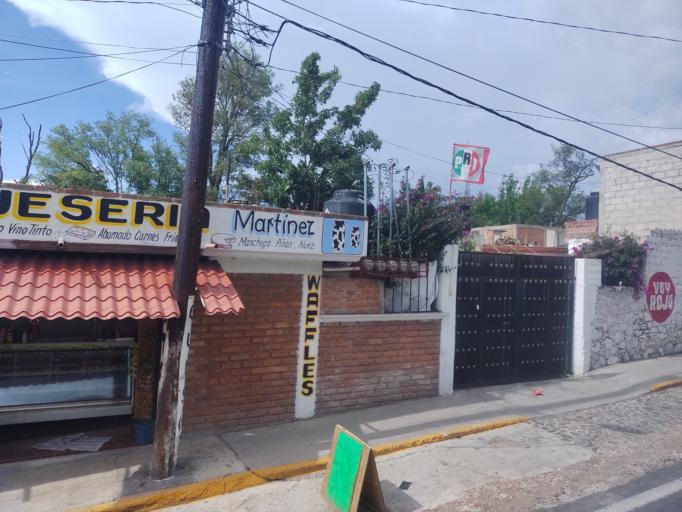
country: MX
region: Mexico
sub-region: Aculco
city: El Colorado
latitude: 20.1070
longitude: -99.7212
